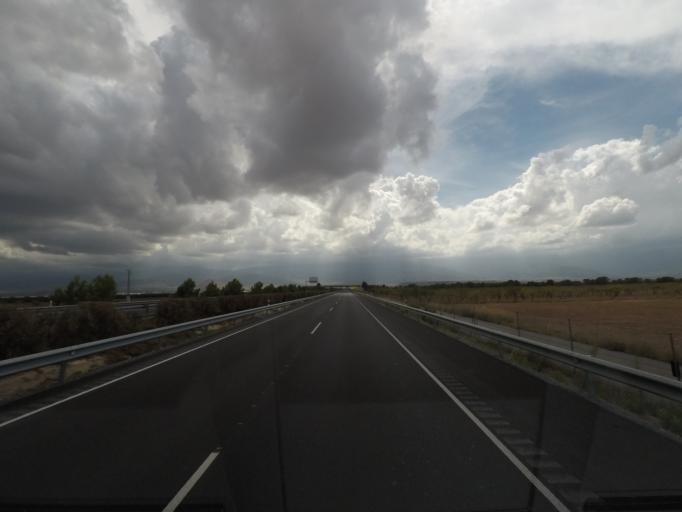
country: ES
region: Andalusia
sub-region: Provincia de Granada
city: Albunan
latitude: 37.2501
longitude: -3.0817
